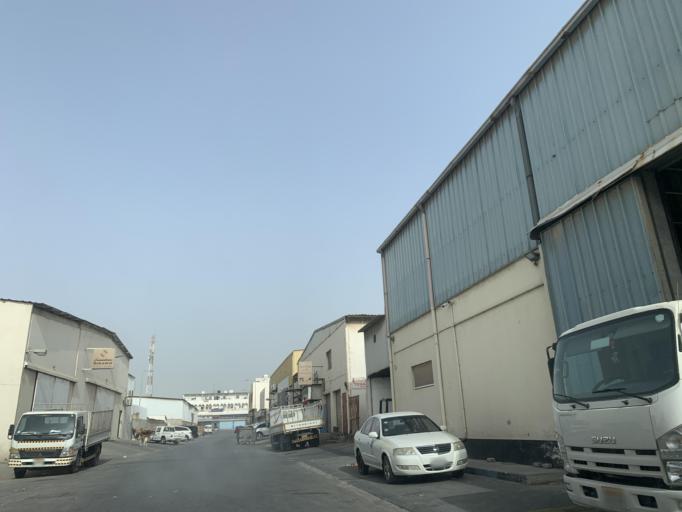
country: BH
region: Northern
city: Madinat `Isa
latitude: 26.1769
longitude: 50.5320
